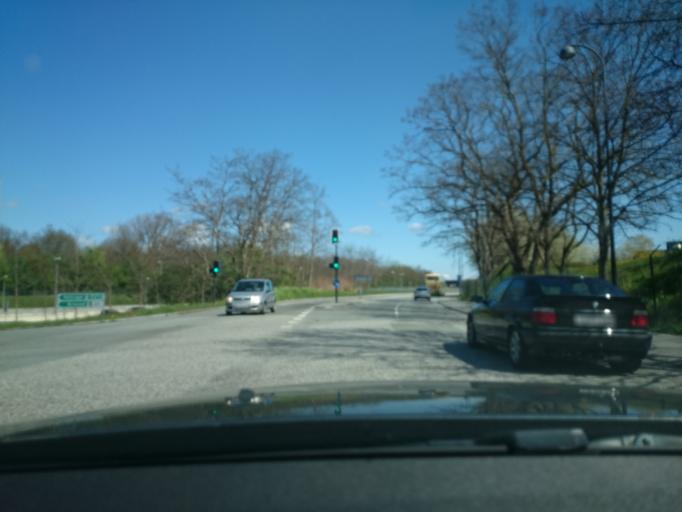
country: DK
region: Capital Region
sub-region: Lyngby-Tarbaek Kommune
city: Kongens Lyngby
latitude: 55.7564
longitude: 12.5122
